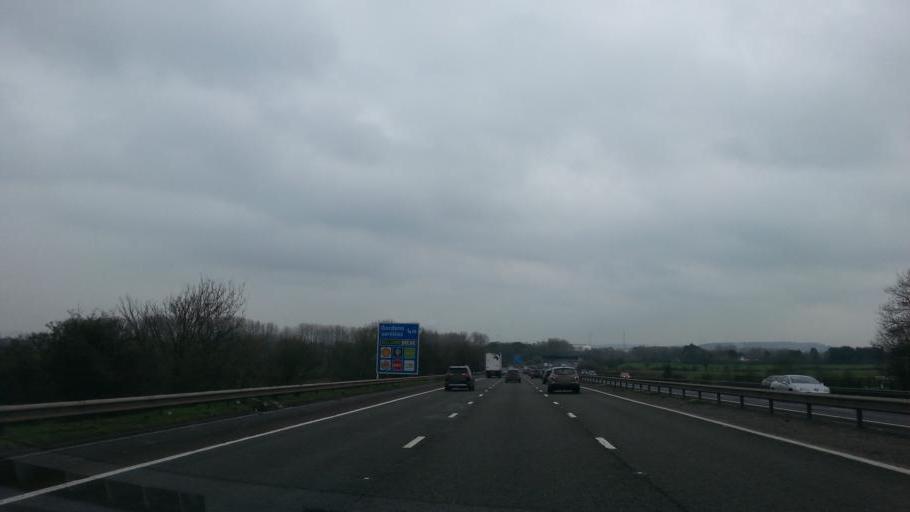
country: GB
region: England
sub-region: North Somerset
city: Easton-in-Gordano
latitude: 51.4720
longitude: -2.7353
